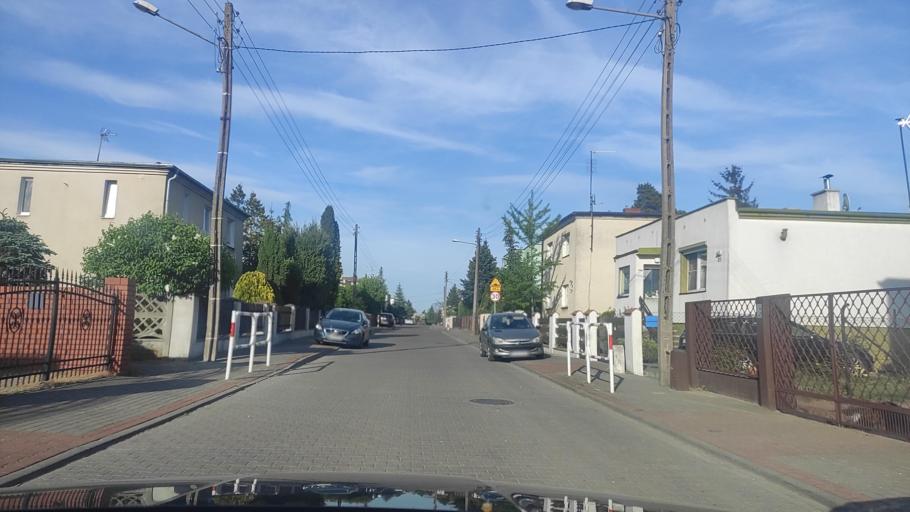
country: PL
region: Greater Poland Voivodeship
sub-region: Powiat poznanski
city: Czerwonak
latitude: 52.4295
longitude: 17.0215
